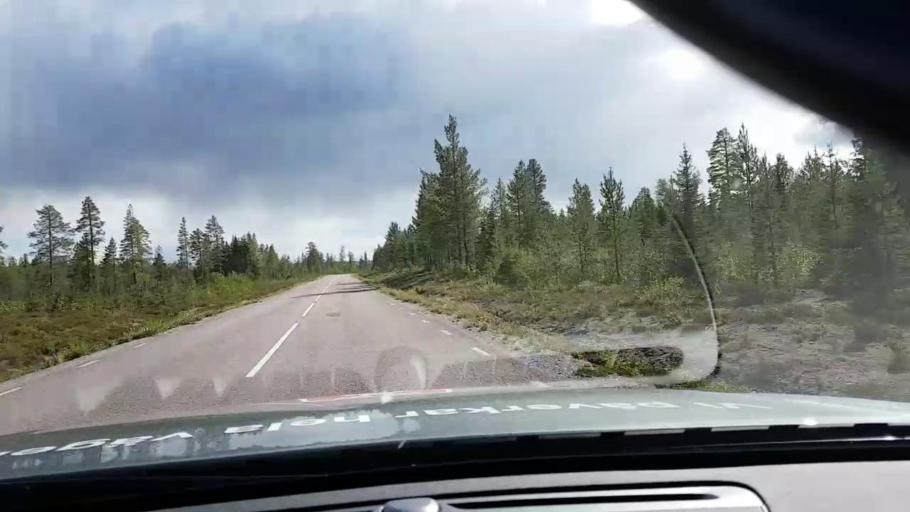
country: SE
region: Vaesterbotten
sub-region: Asele Kommun
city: Asele
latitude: 63.8985
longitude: 17.3491
